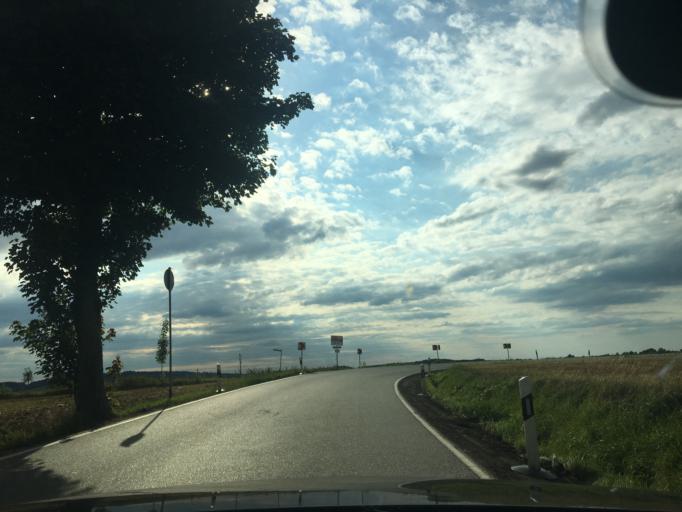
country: DE
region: Saxony
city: Oelsnitz
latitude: 50.6956
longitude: 12.6844
